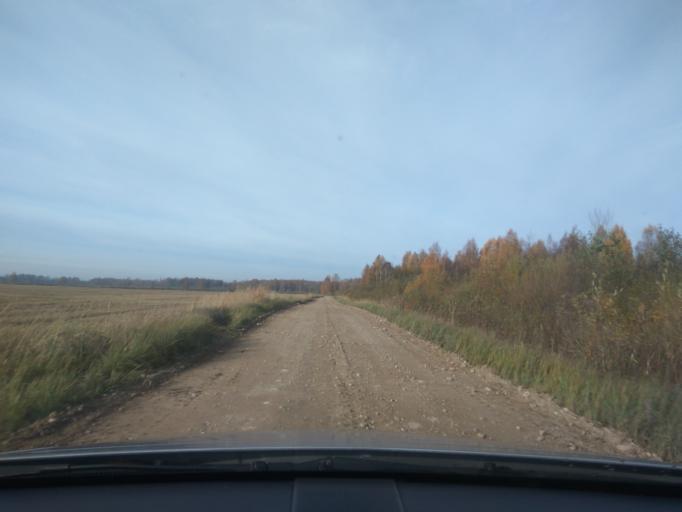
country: LV
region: Aizpute
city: Aizpute
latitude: 56.8458
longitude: 21.7007
